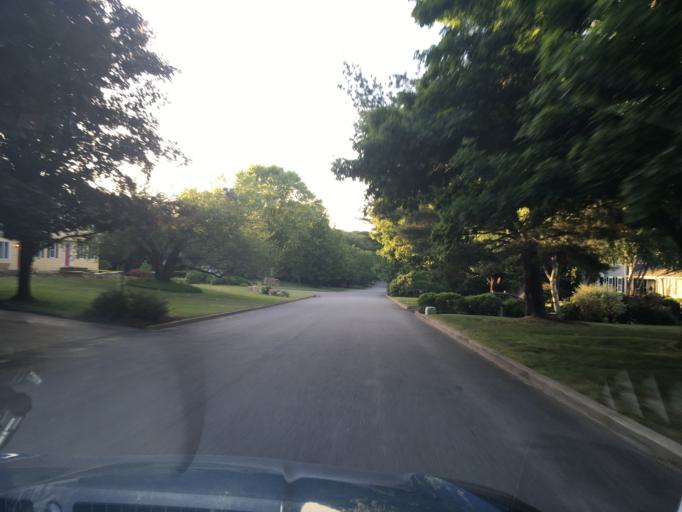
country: US
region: Rhode Island
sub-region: Kent County
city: East Greenwich
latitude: 41.6269
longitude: -71.5005
